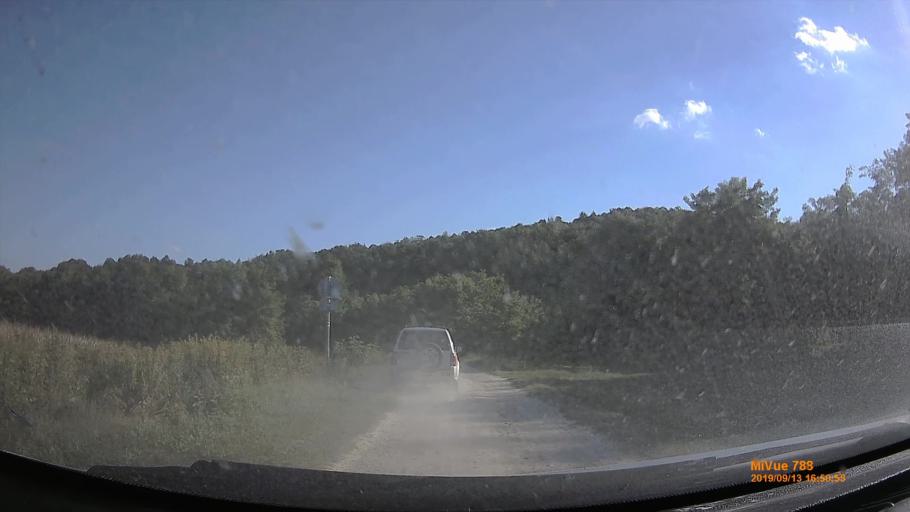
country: HU
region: Zala
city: Pacsa
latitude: 46.6054
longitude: 17.0656
